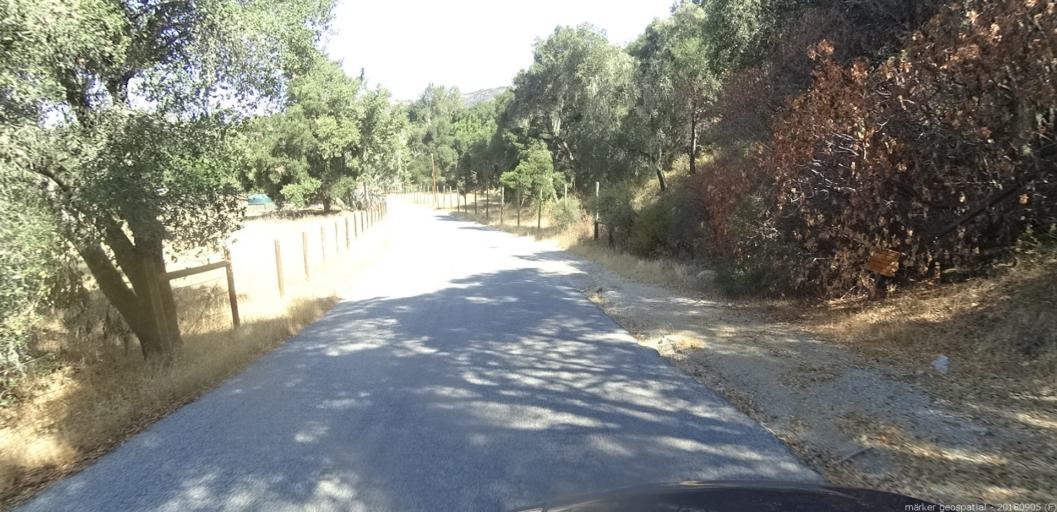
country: US
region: California
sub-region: Monterey County
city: Carmel Valley Village
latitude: 36.4063
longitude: -121.6643
